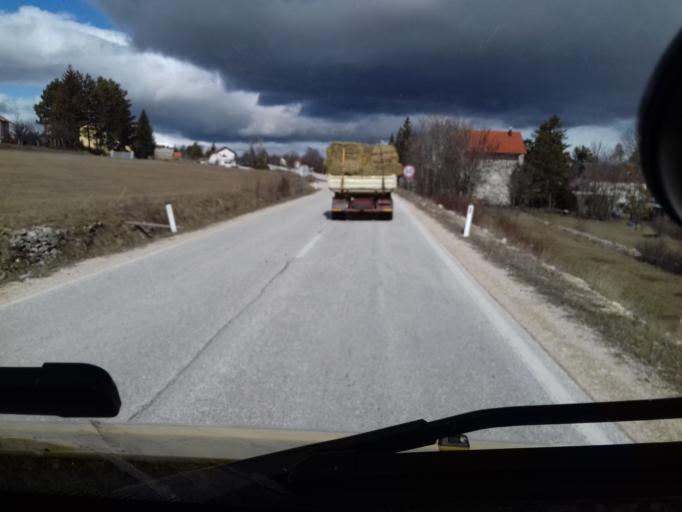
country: BA
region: Federation of Bosnia and Herzegovina
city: Dreznica
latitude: 43.6015
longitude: 17.2736
